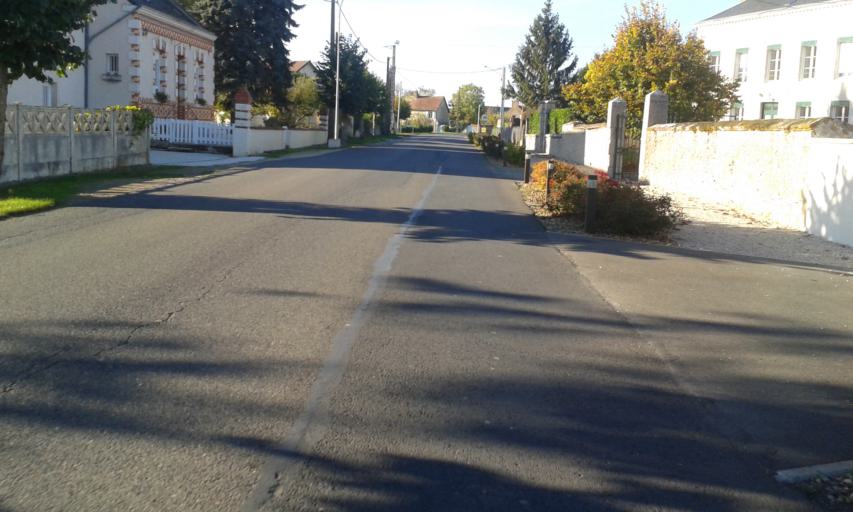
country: FR
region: Centre
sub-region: Departement du Loir-et-Cher
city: Oucques
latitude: 47.8291
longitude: 1.3843
